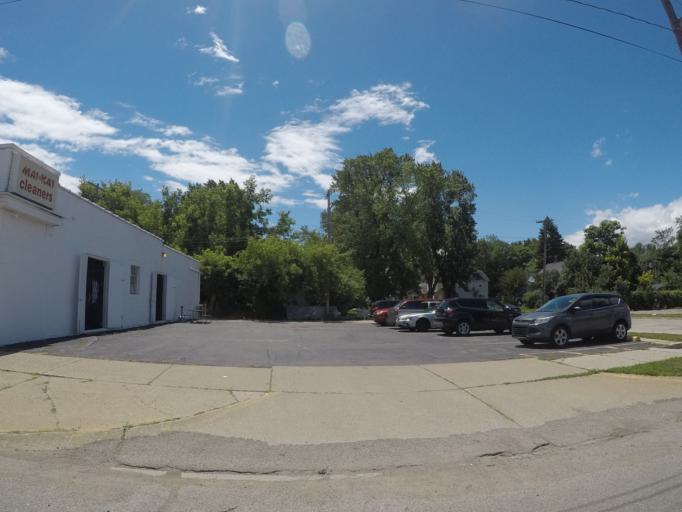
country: US
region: Michigan
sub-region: Wayne County
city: Redford
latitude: 42.4287
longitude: -83.2803
